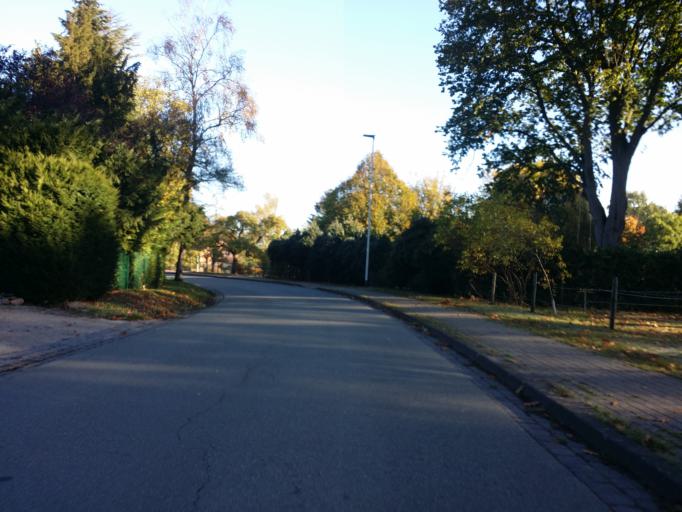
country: DE
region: Lower Saxony
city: Grasberg
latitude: 53.1911
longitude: 9.0198
